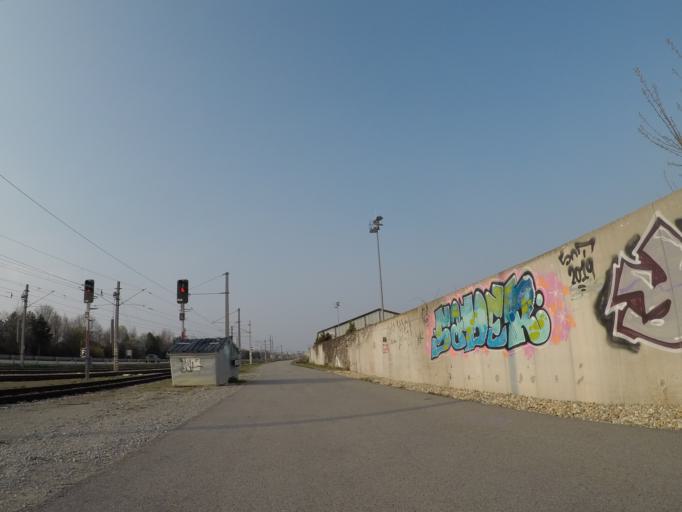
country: AT
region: Lower Austria
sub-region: Politischer Bezirk Modling
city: Wiener Neudorf
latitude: 48.0888
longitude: 16.3147
